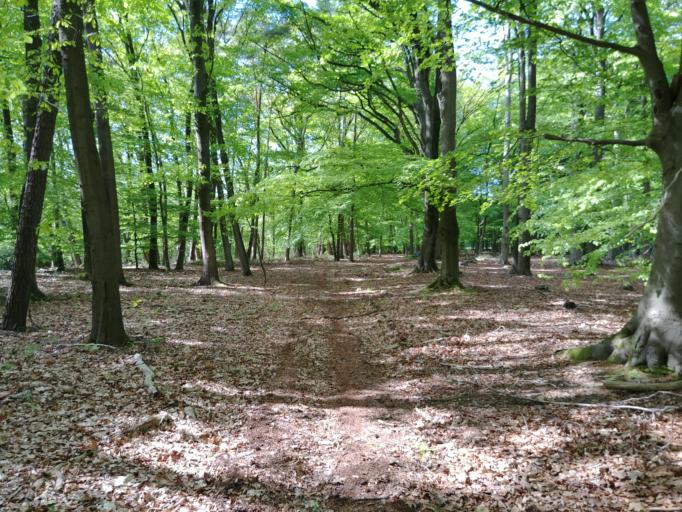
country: NL
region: Gelderland
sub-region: Gemeente Apeldoorn
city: Uddel
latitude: 52.2937
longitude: 5.7267
